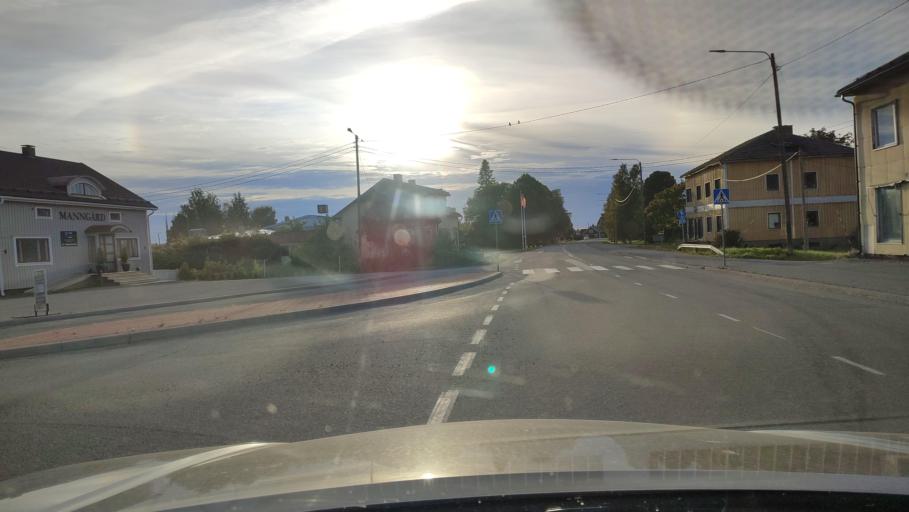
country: FI
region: Ostrobothnia
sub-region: Sydosterbotten
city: Kristinestad
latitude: 62.2547
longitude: 21.5081
